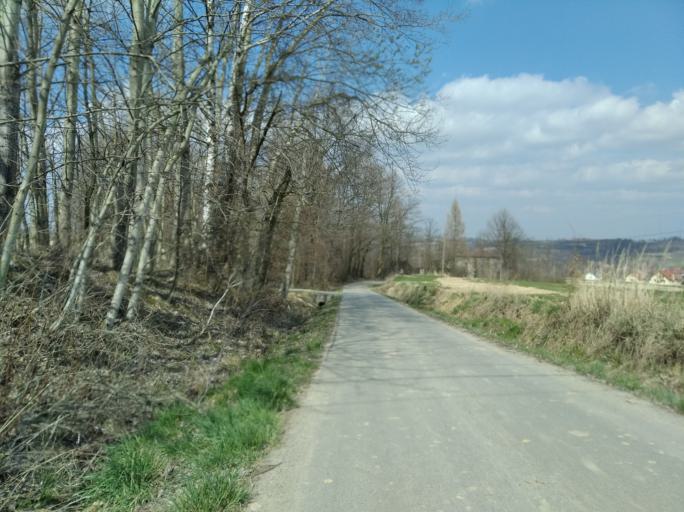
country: PL
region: Subcarpathian Voivodeship
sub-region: Powiat strzyzowski
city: Strzyzow
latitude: 49.8366
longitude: 21.8081
